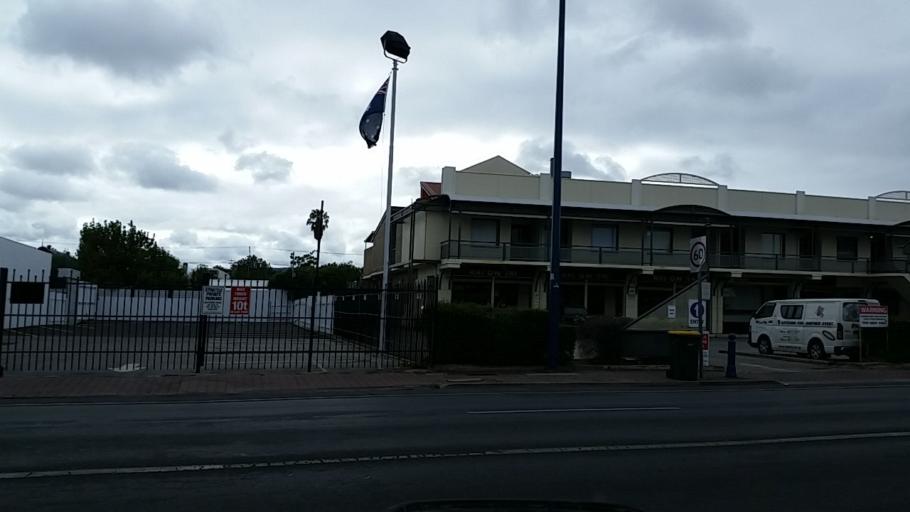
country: AU
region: South Australia
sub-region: Unley
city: Unley
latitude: -34.9423
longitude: 138.6067
